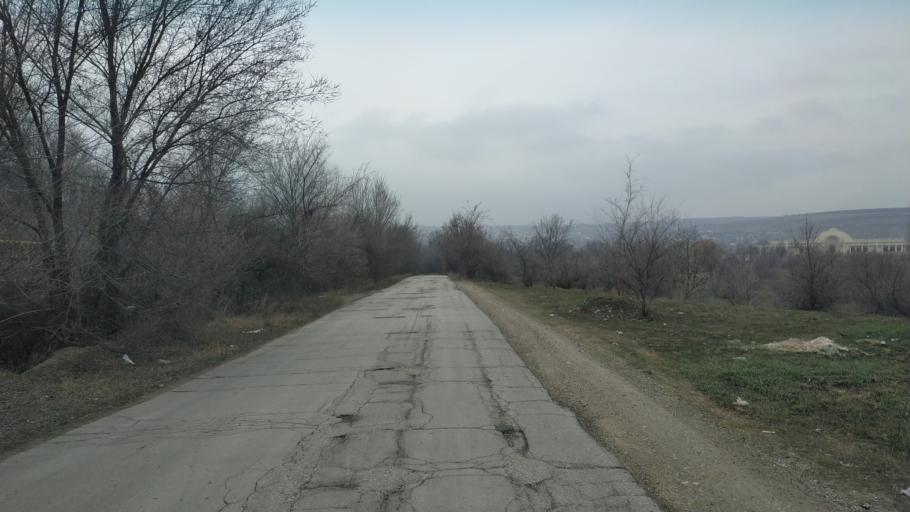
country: MD
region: Chisinau
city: Singera
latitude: 46.9223
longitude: 29.0049
